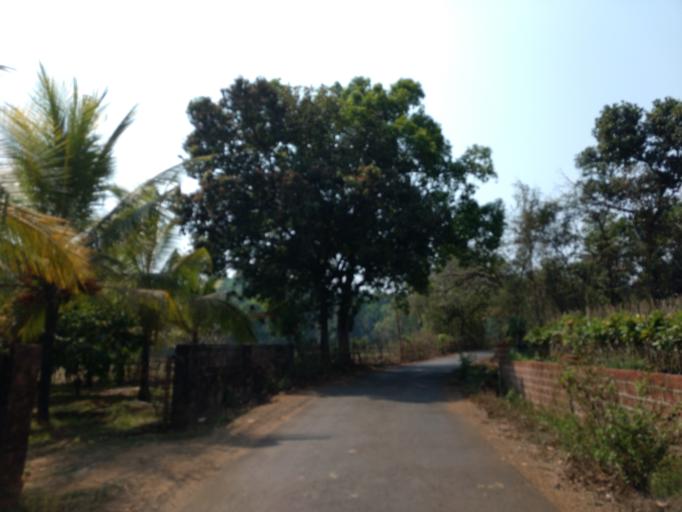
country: IN
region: Maharashtra
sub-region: Sindhudurg
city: Kudal
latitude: 16.0384
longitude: 73.6827
